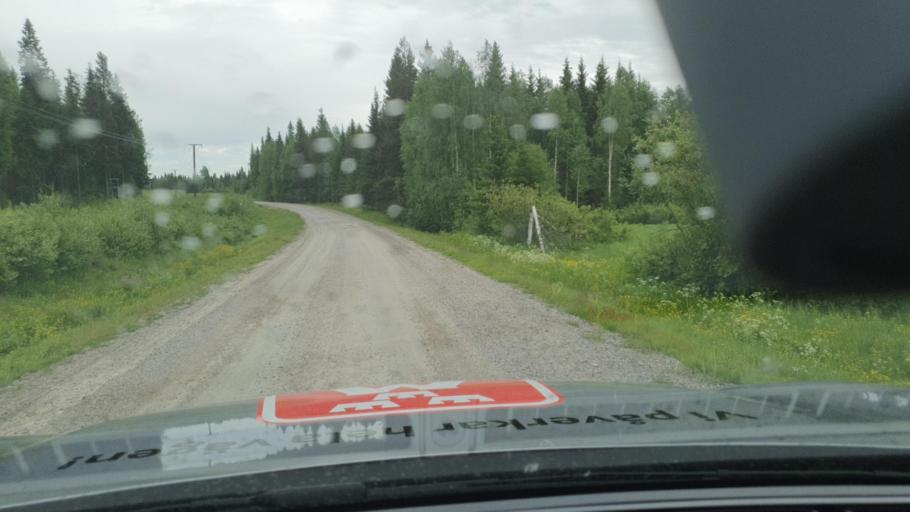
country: SE
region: Norrbotten
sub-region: Kalix Kommun
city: Rolfs
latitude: 66.0338
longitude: 23.0663
